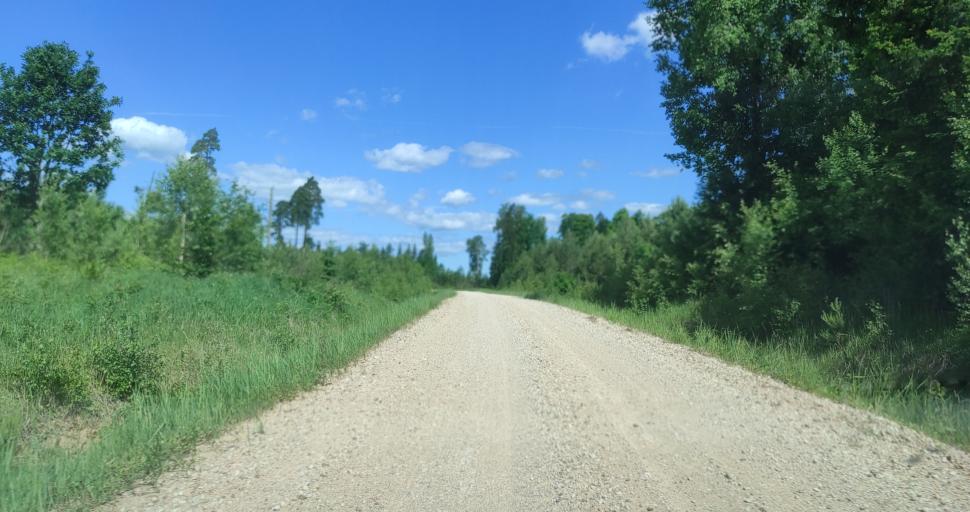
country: LV
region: Kuldigas Rajons
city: Kuldiga
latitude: 56.9460
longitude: 21.7888
